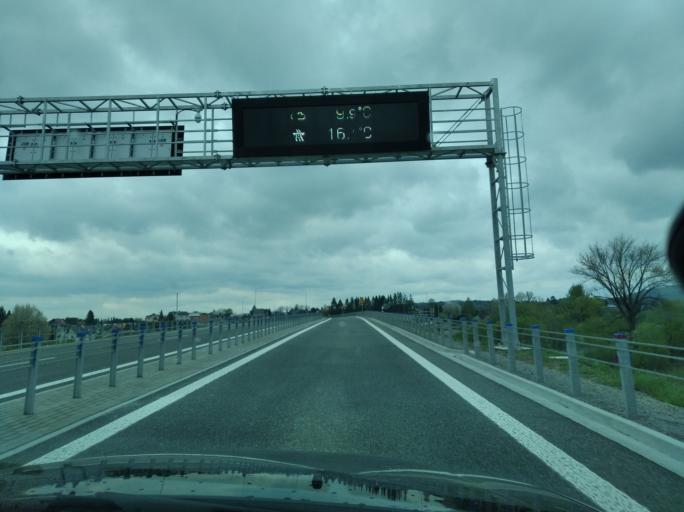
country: PL
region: Subcarpathian Voivodeship
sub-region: Powiat sanocki
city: Sanok
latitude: 49.5669
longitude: 22.1522
